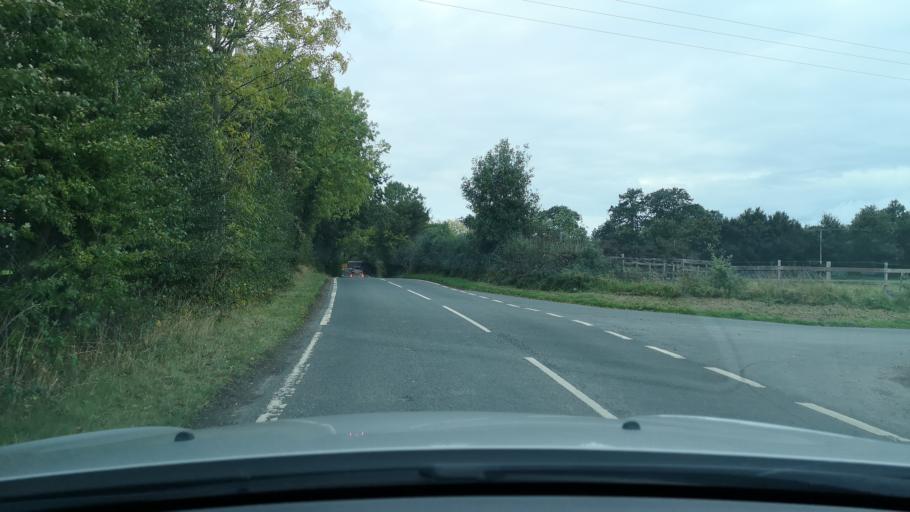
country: GB
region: England
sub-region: City and Borough of Wakefield
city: Low Ackworth
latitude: 53.6581
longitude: -1.3111
